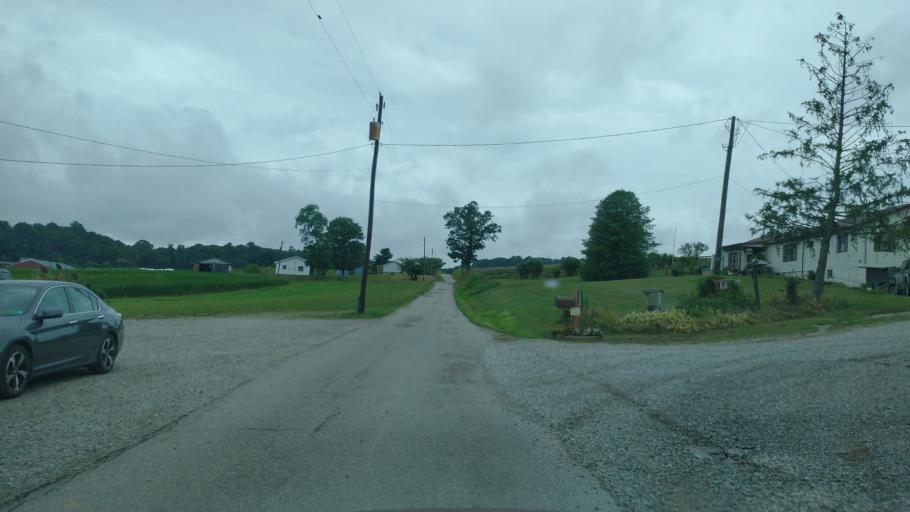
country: US
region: West Virginia
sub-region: Mason County
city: New Haven
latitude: 38.9246
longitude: -81.9708
